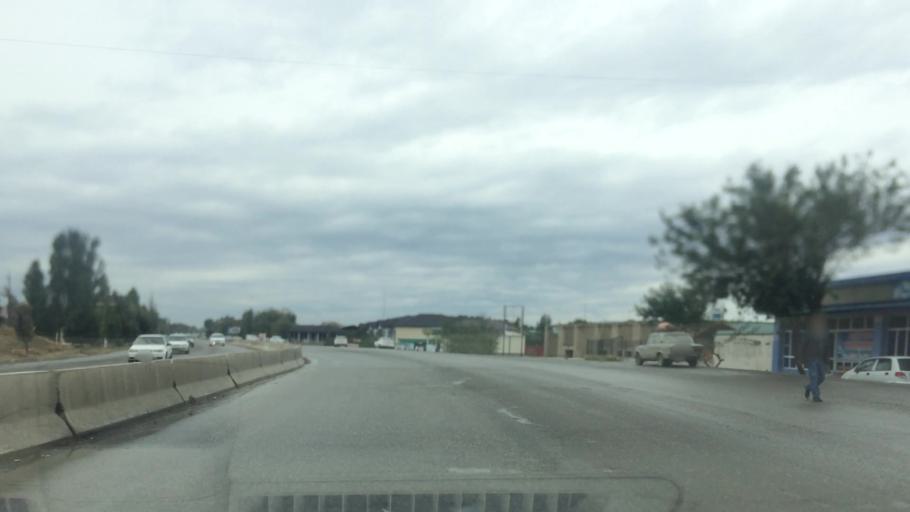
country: UZ
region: Jizzax
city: Jizzax
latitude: 40.0112
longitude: 67.6004
